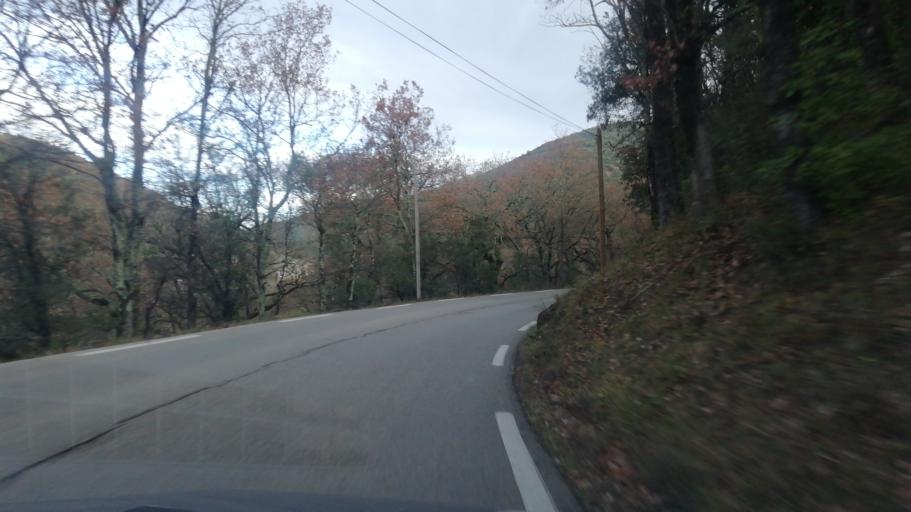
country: FR
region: Languedoc-Roussillon
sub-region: Departement du Gard
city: Saint-Hippolyte-du-Fort
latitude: 43.9820
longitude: 3.8516
